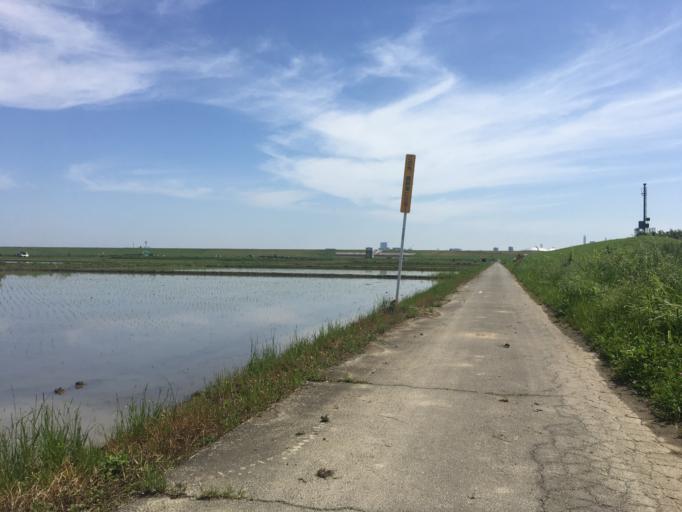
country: JP
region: Saitama
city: Shiki
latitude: 35.8755
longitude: 139.5773
